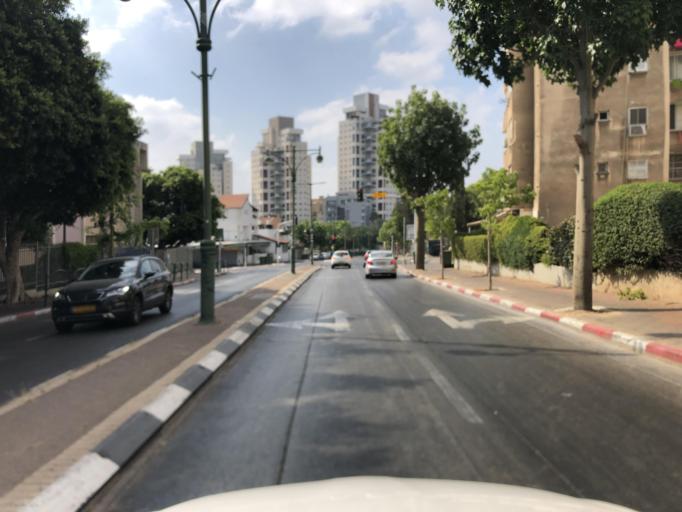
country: IL
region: Tel Aviv
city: Bene Beraq
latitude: 32.0668
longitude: 34.8328
